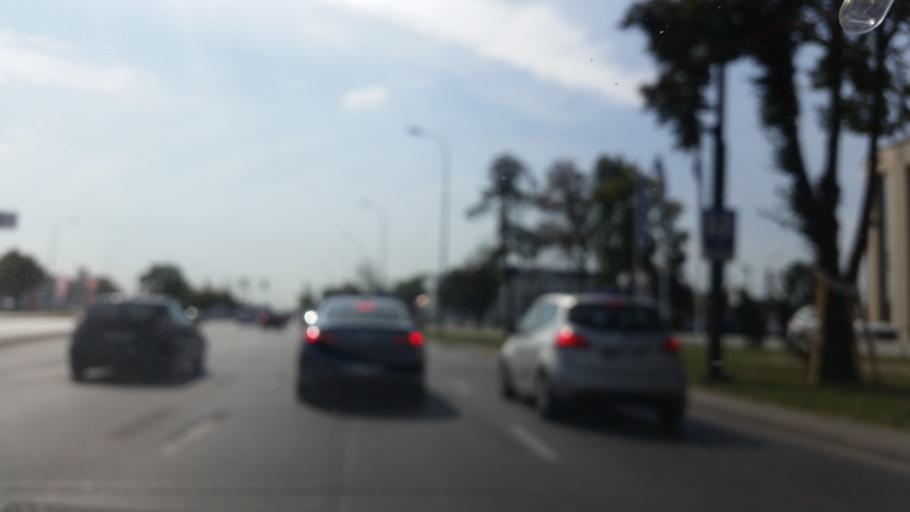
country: PL
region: Masovian Voivodeship
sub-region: Powiat piaseczynski
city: Mysiadlo
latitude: 52.1072
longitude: 21.0184
